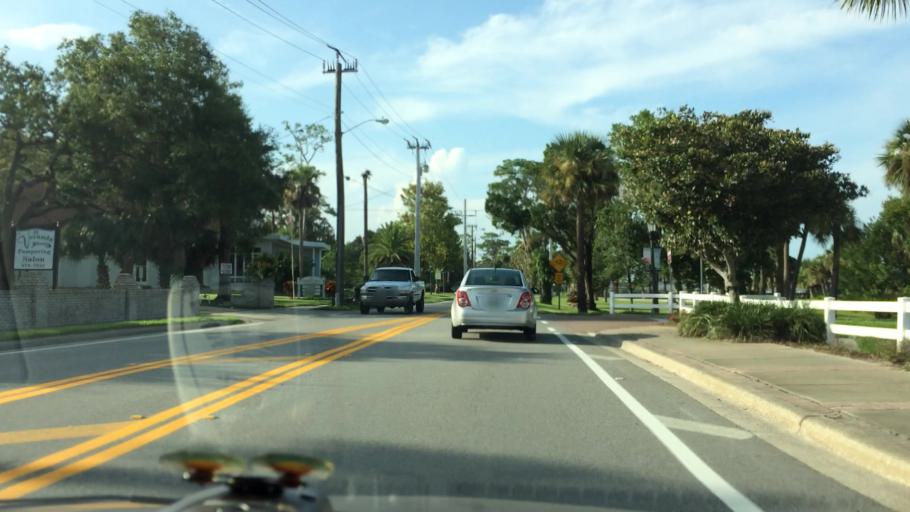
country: US
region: Florida
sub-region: Volusia County
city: Ormond Beach
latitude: 29.2867
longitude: -81.0559
